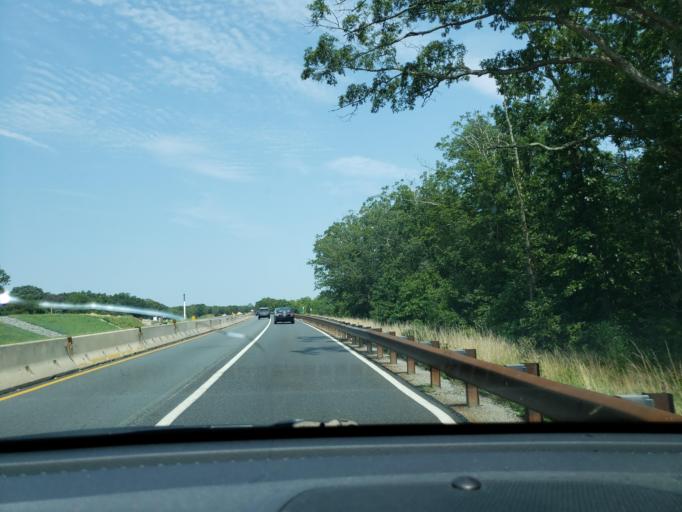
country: US
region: New Jersey
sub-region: Atlantic County
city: Linwood
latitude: 39.3465
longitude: -74.5994
